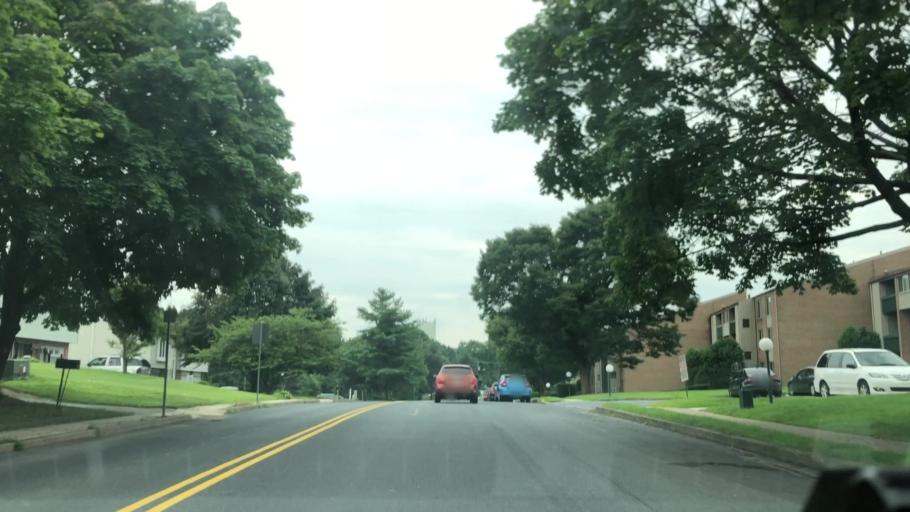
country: US
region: Pennsylvania
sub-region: Dauphin County
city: Colonial Park
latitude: 40.2865
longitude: -76.8103
